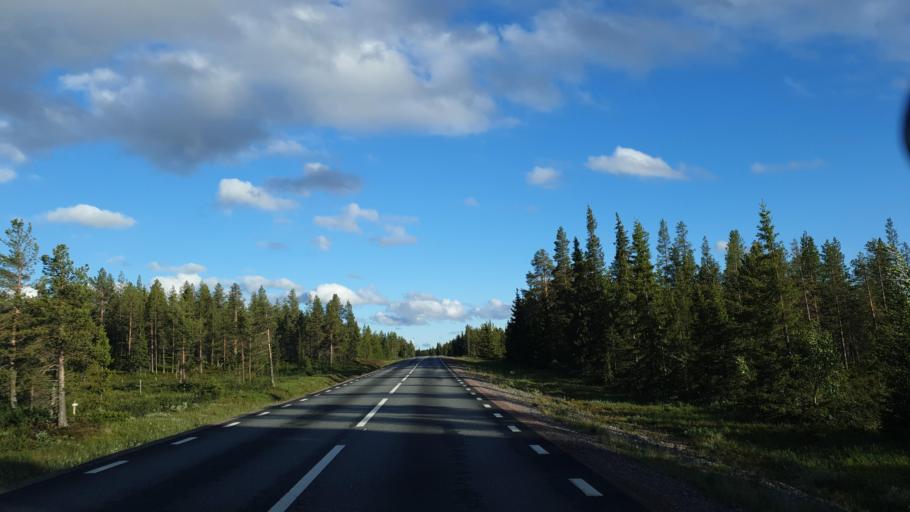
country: SE
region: Norrbotten
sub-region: Arjeplogs Kommun
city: Arjeplog
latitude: 65.8772
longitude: 18.4067
